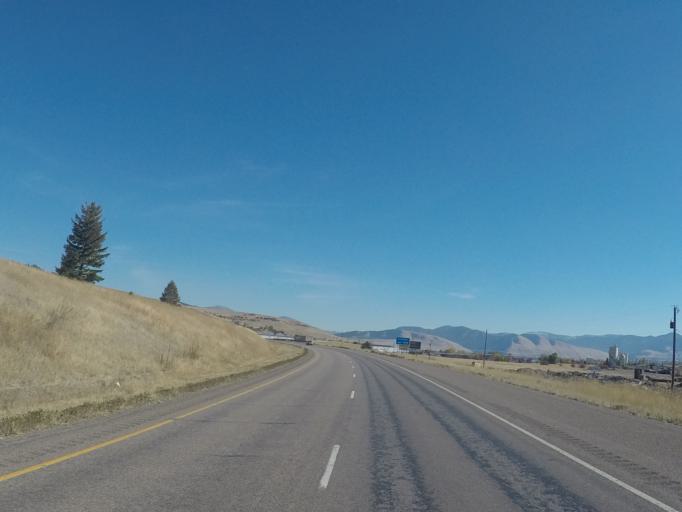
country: US
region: Montana
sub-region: Missoula County
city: Orchard Homes
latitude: 46.9393
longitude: -114.1100
